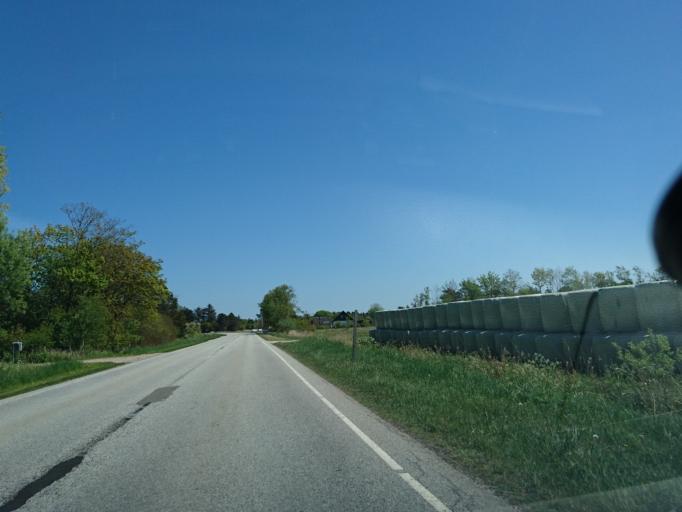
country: DK
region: North Denmark
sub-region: Hjorring Kommune
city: Sindal
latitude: 57.5882
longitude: 10.2783
